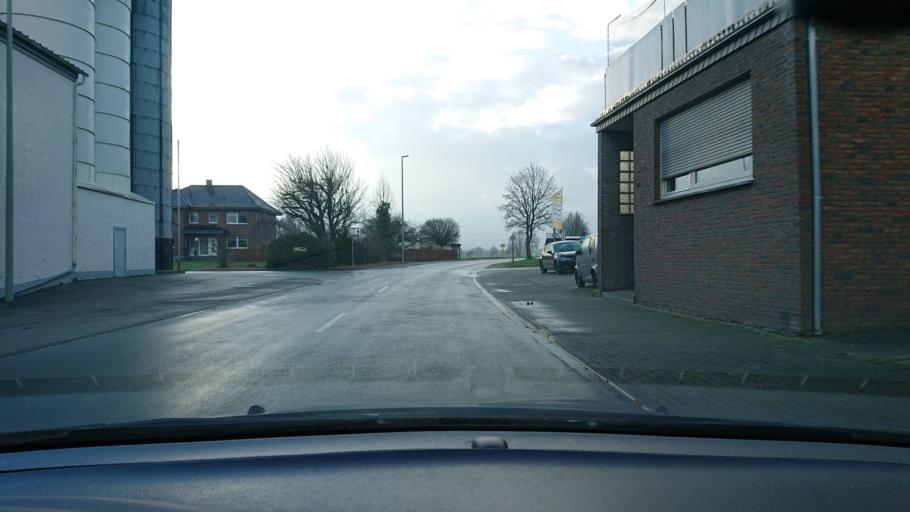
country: DE
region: North Rhine-Westphalia
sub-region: Regierungsbezirk Arnsberg
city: Bad Sassendorf
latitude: 51.6109
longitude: 8.2452
